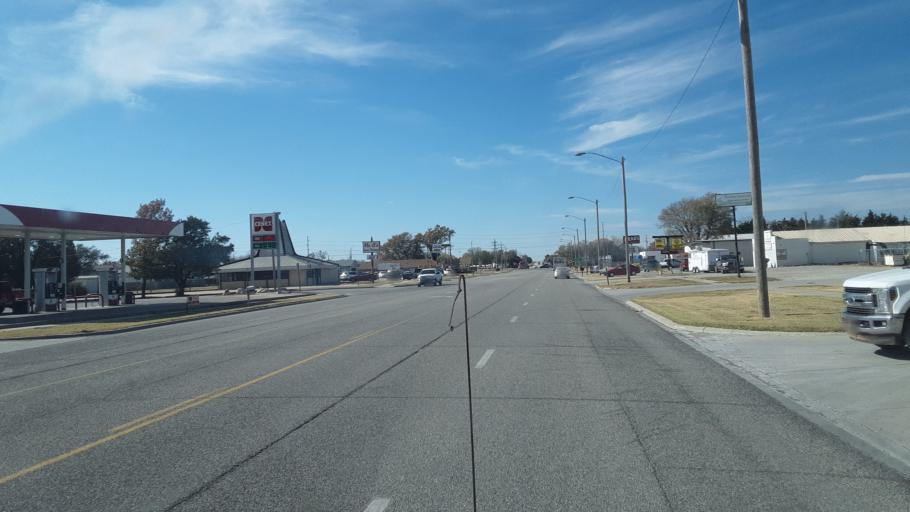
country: US
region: Kansas
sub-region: McPherson County
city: McPherson
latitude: 38.3695
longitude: -97.6892
